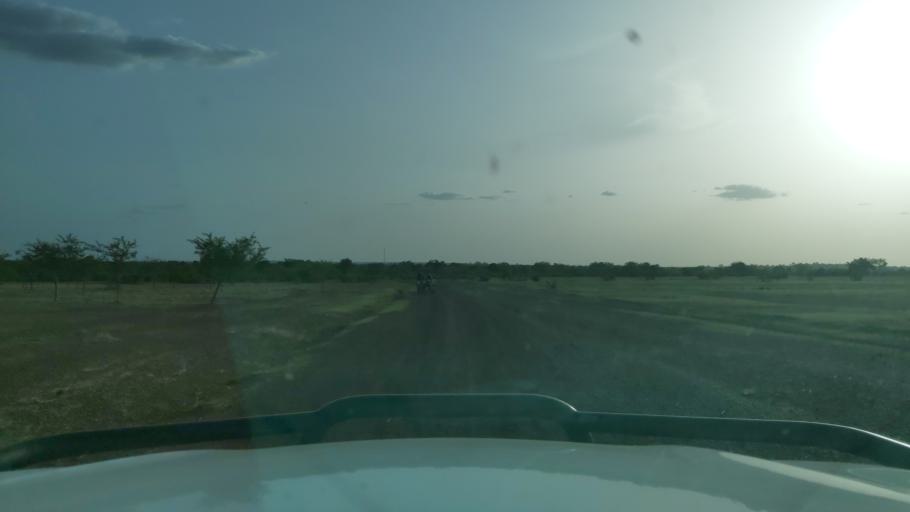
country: ML
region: Koulikoro
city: Kolokani
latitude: 13.2082
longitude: -7.9107
